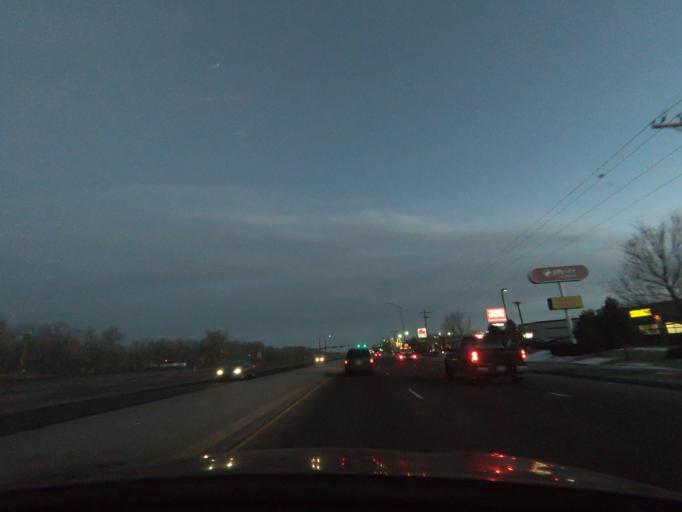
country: US
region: Colorado
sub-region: El Paso County
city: Security-Widefield
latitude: 38.7439
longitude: -104.7375
